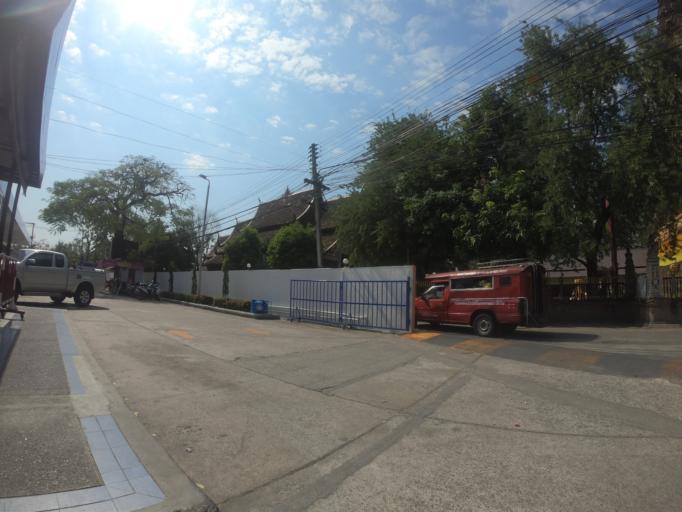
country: TH
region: Chiang Mai
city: Chiang Mai
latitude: 18.7965
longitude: 98.9830
